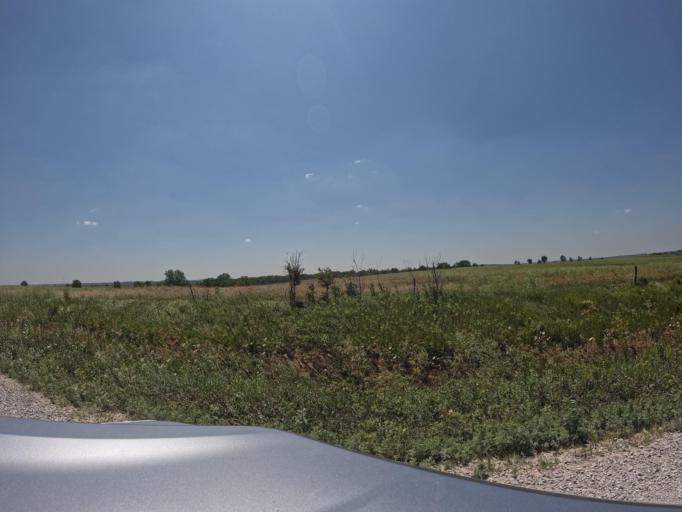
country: US
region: Iowa
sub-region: Keokuk County
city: Sigourney
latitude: 41.2577
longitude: -92.1843
